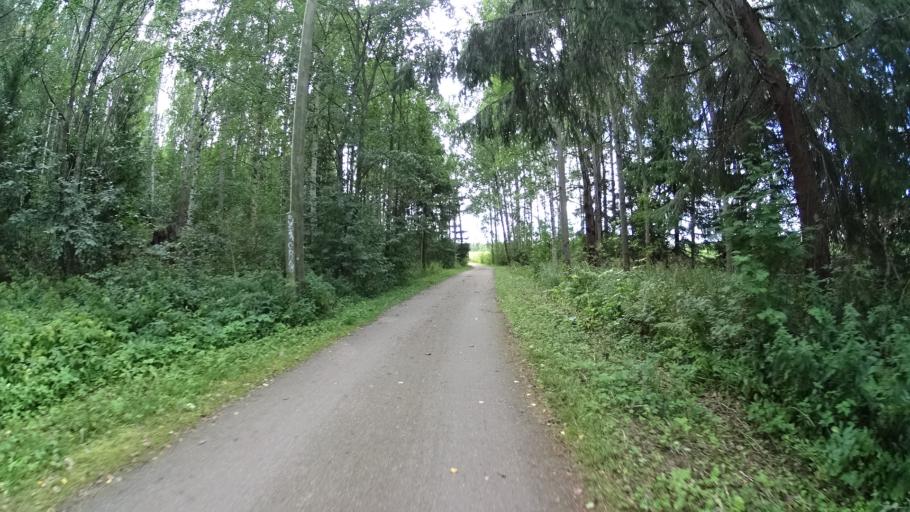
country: FI
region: Uusimaa
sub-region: Helsinki
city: Teekkarikylae
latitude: 60.2645
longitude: 24.9003
